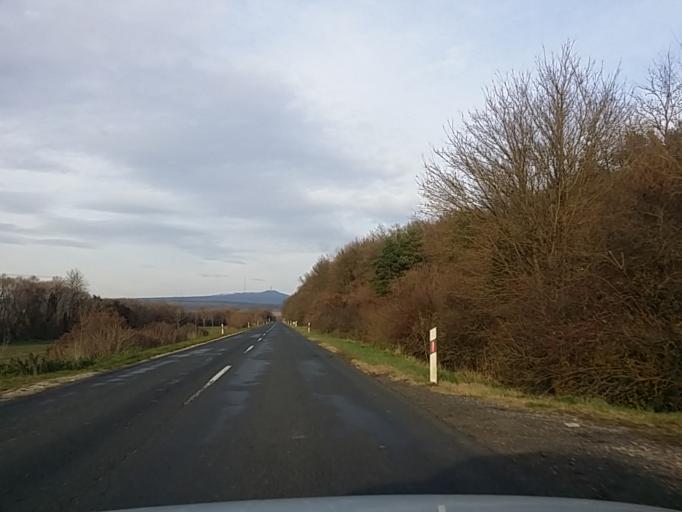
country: HU
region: Veszprem
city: Urkut
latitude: 46.9823
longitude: 17.6284
